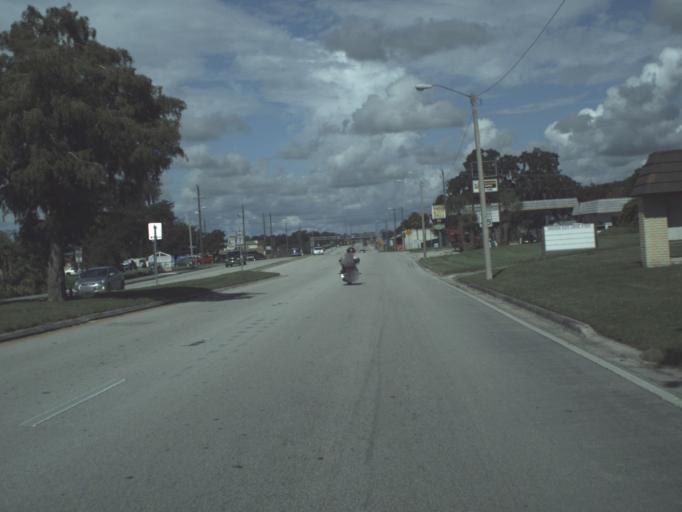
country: US
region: Florida
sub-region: DeSoto County
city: Arcadia
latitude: 27.2196
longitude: -81.8719
